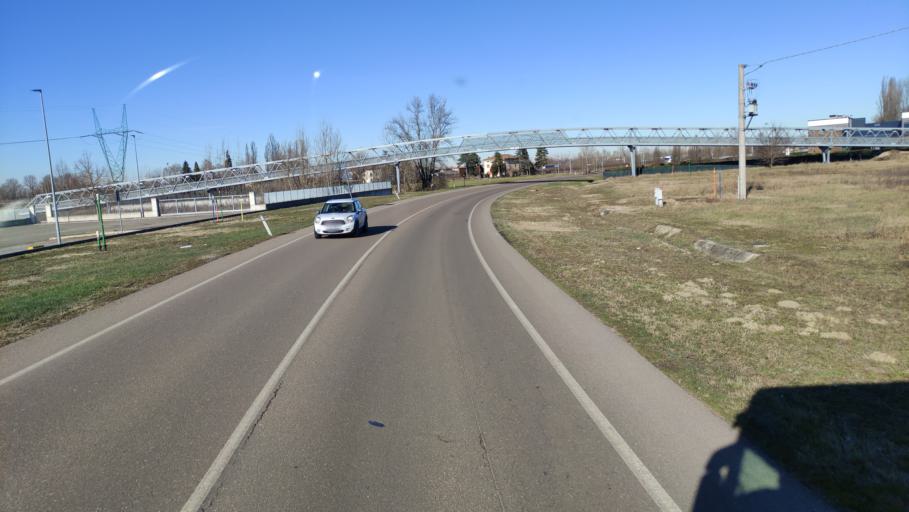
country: IT
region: Emilia-Romagna
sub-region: Provincia di Reggio Emilia
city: Correggio
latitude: 44.7674
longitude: 10.8116
